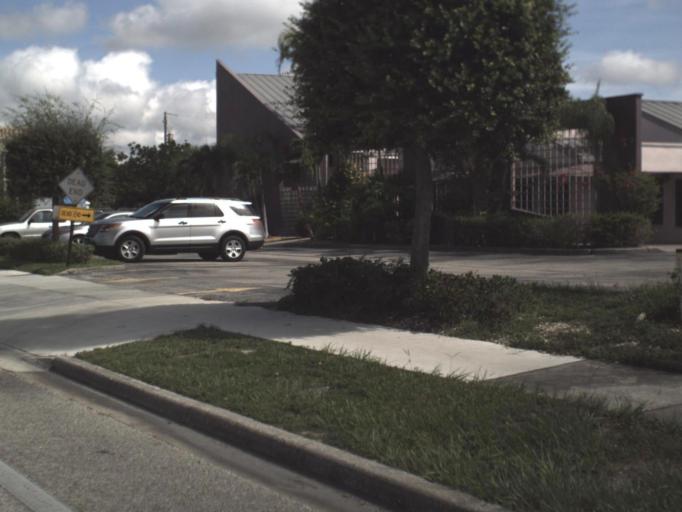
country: US
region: Florida
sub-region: Manatee County
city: Whitfield
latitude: 27.3970
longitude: -82.5633
